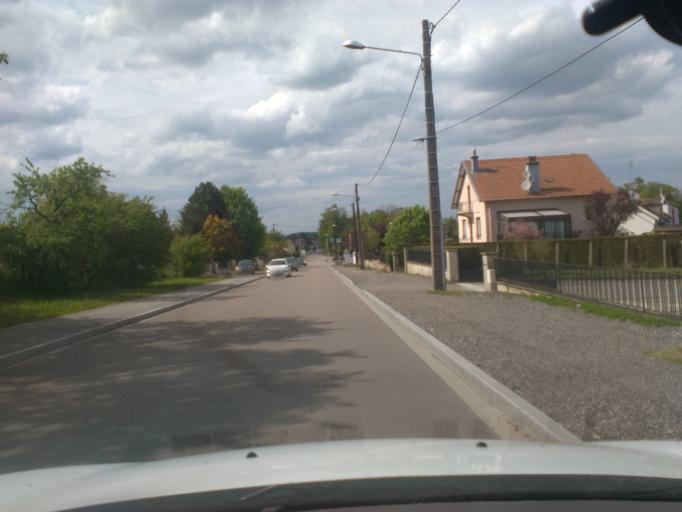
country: FR
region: Lorraine
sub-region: Departement des Vosges
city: Mirecourt
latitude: 48.2688
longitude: 6.1403
